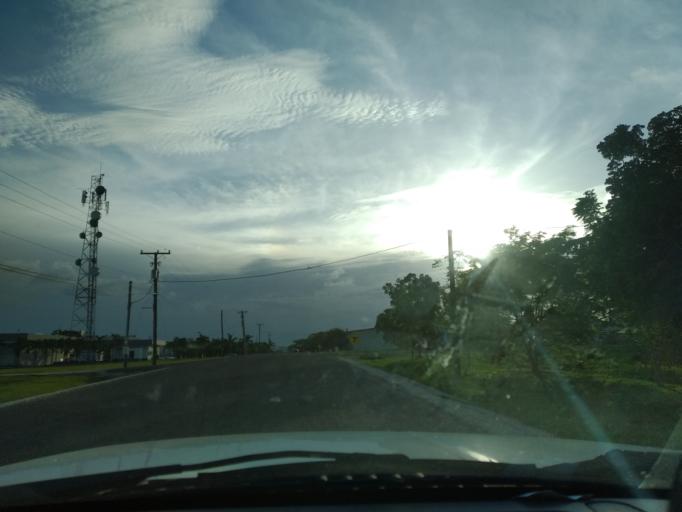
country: BZ
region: Cayo
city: San Ignacio
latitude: 17.2568
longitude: -89.0004
